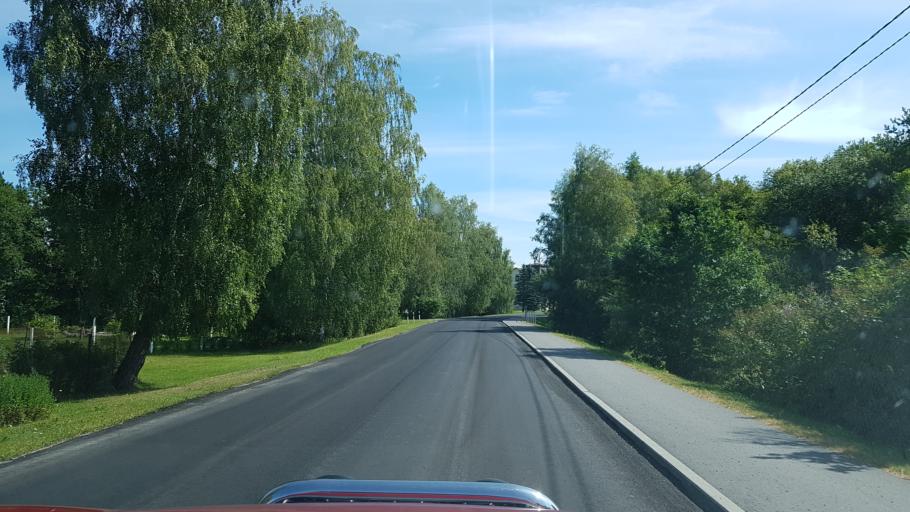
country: EE
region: Laeaene-Virumaa
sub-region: Tapa vald
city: Tapa
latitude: 59.1929
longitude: 25.8340
